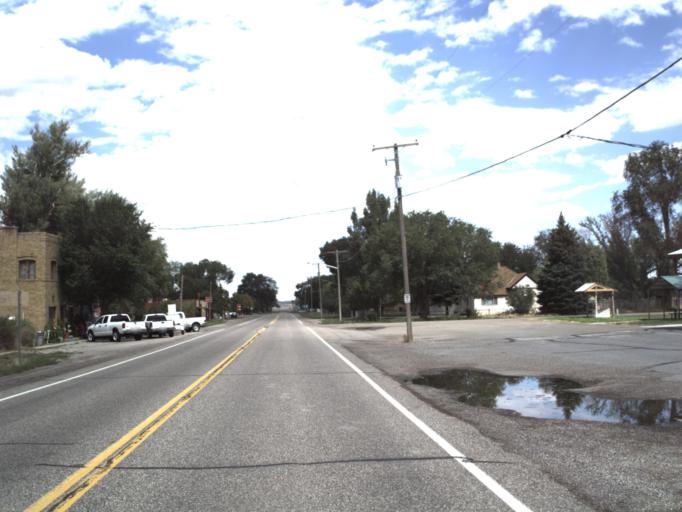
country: US
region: Utah
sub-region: Sanpete County
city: Gunnison
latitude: 39.2455
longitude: -112.1039
